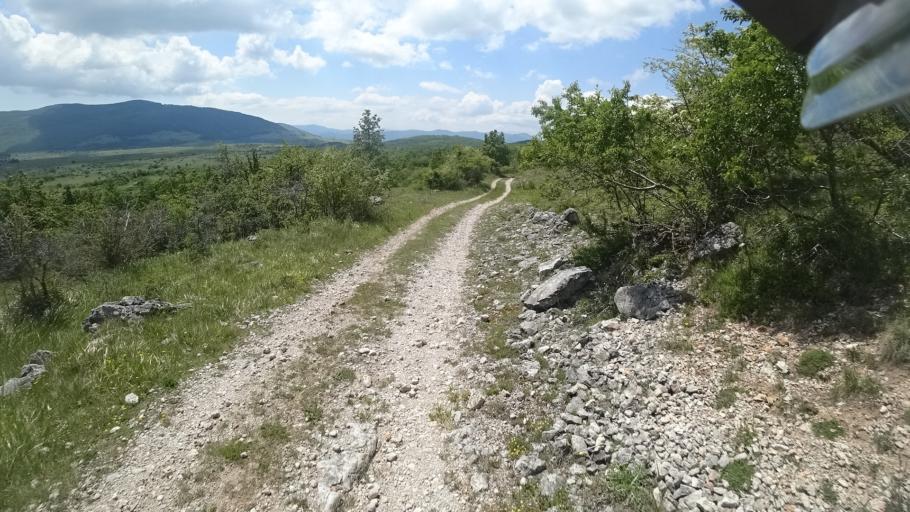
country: HR
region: Zadarska
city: Gracac
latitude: 44.3673
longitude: 15.9523
